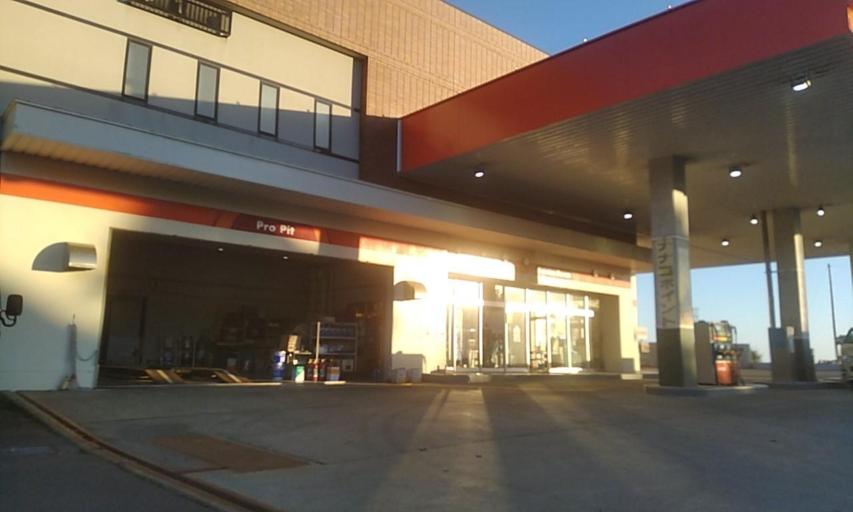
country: JP
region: Hokkaido
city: Shizunai-furukawacho
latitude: 42.1272
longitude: 142.9263
